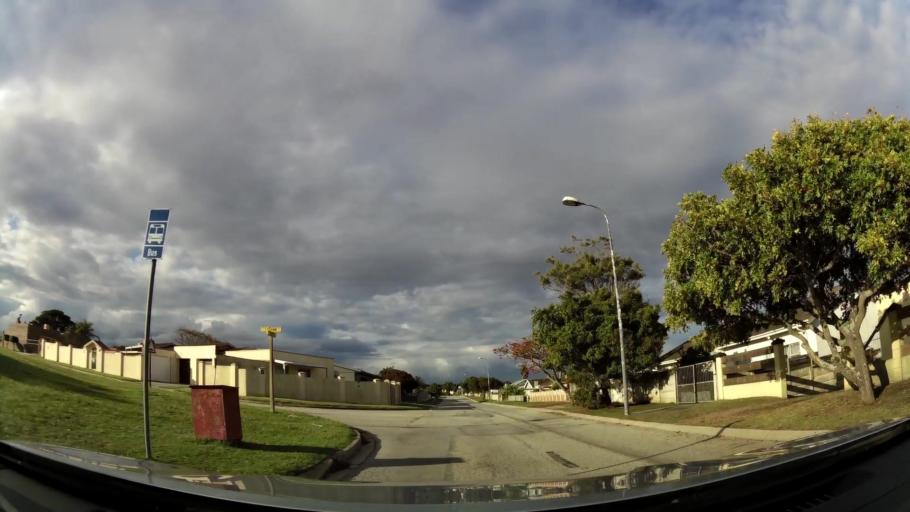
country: ZA
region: Eastern Cape
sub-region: Nelson Mandela Bay Metropolitan Municipality
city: Port Elizabeth
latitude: -33.9483
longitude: 25.4805
